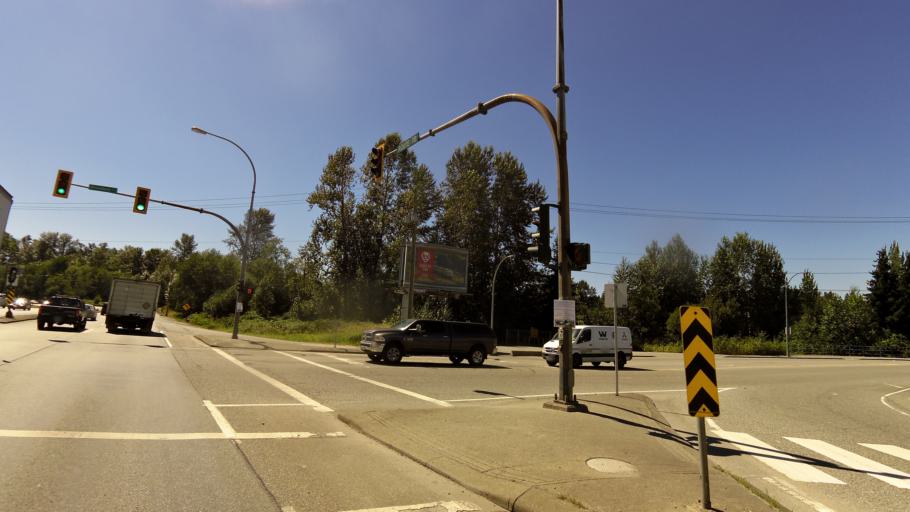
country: CA
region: British Columbia
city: Coquitlam
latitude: 49.2410
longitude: -122.7617
